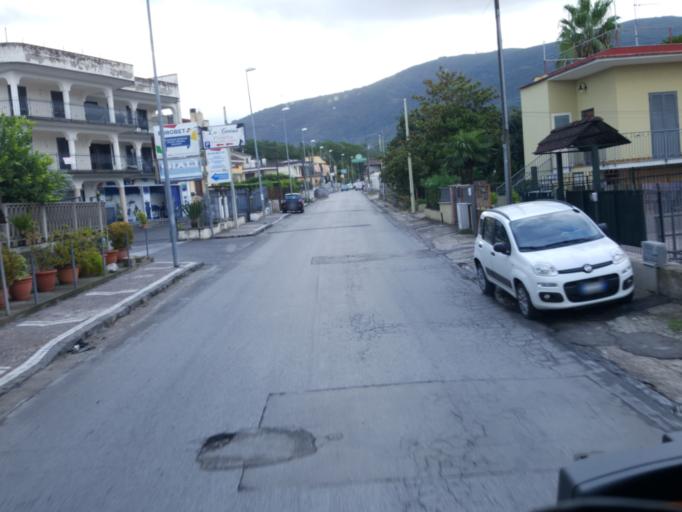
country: IT
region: Campania
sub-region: Provincia di Napoli
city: Palma Campania
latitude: 40.8790
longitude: 14.5565
